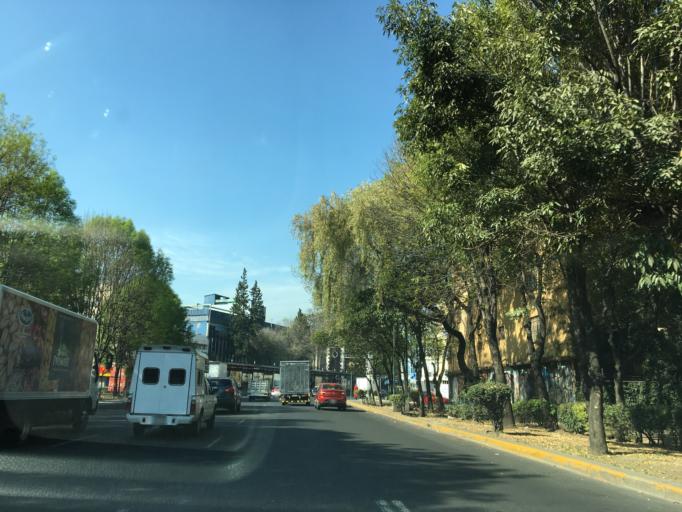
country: MX
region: Mexico City
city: Benito Juarez
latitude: 19.4057
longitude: -99.1764
